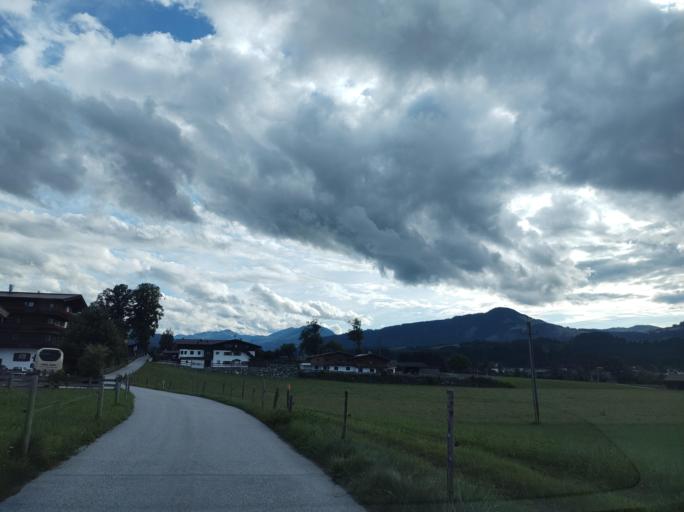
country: AT
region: Tyrol
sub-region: Politischer Bezirk Kitzbuhel
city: Oberndorf in Tirol
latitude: 47.4999
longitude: 12.3967
